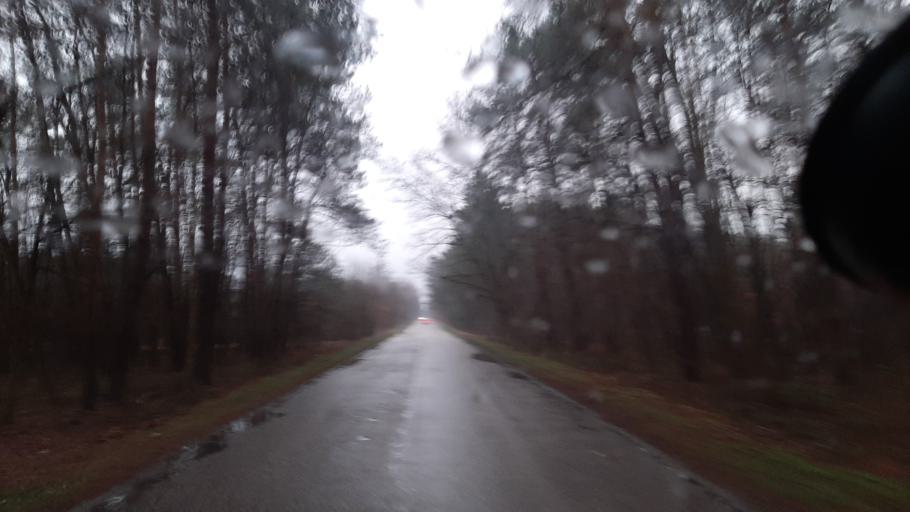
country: PL
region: Lublin Voivodeship
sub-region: Powiat lubartowski
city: Kamionka
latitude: 51.5056
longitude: 22.4891
